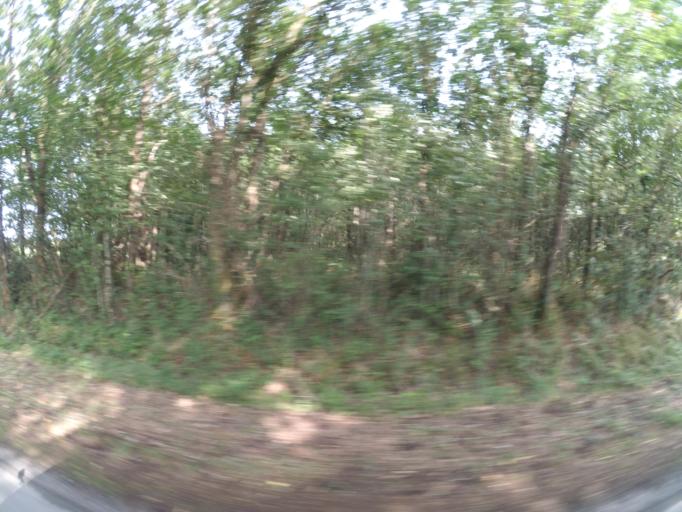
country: FR
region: Pays de la Loire
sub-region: Departement de la Vendee
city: Bouffere
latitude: 46.9416
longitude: -1.3294
